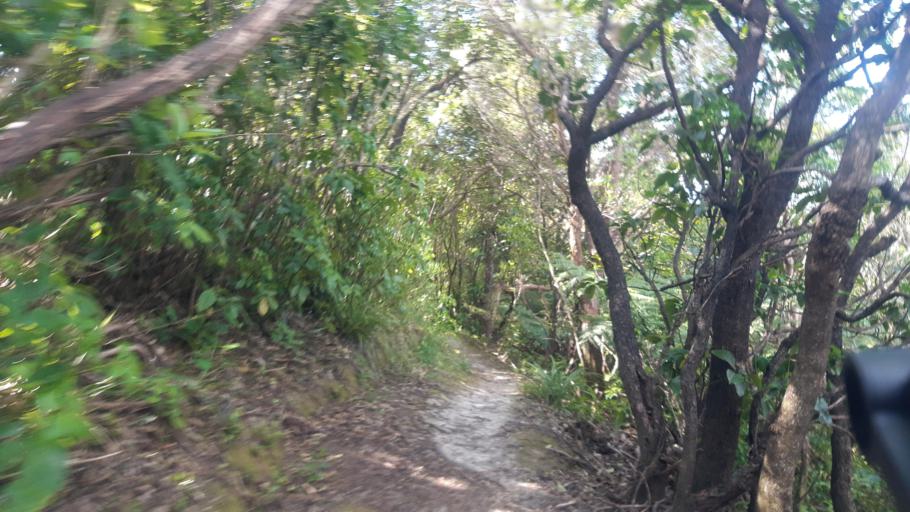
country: NZ
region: Marlborough
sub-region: Marlborough District
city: Picton
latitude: -41.2759
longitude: 174.0189
